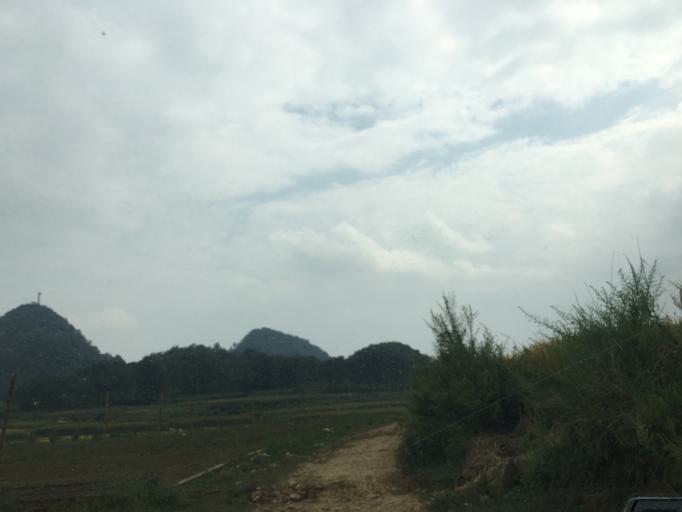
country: CN
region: Guangxi Zhuangzu Zizhiqu
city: Xinzhou
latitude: 25.4919
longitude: 105.6522
